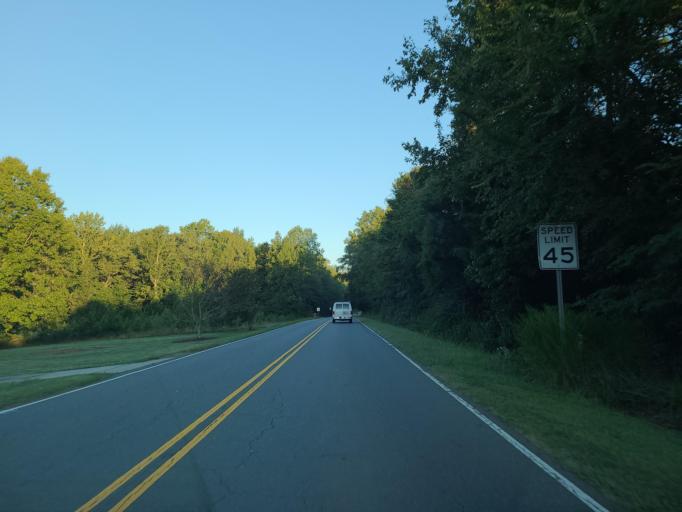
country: US
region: North Carolina
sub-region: Union County
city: Weddington
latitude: 35.0158
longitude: -80.7504
